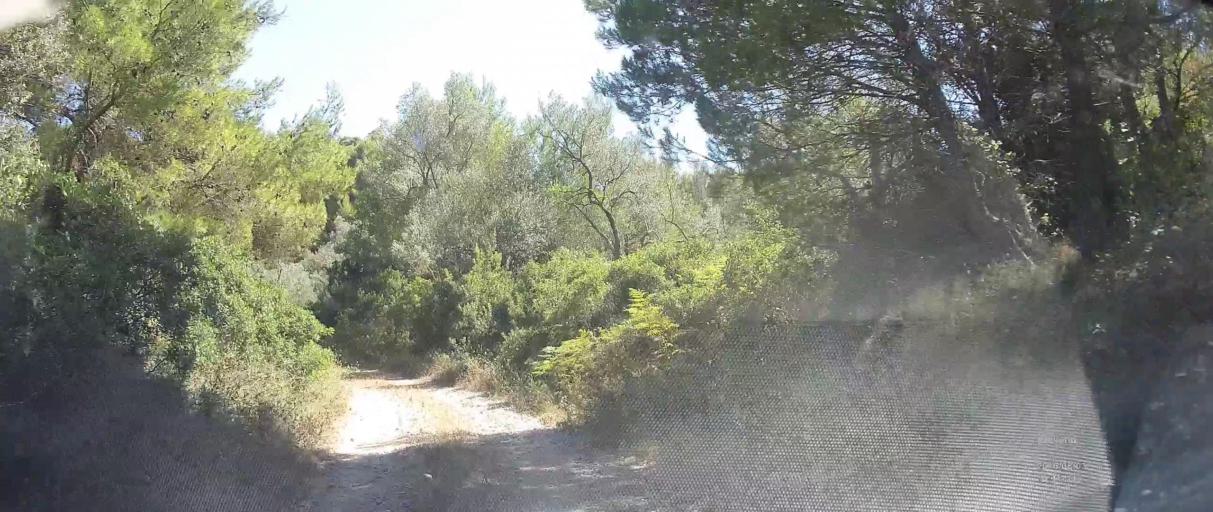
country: HR
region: Dubrovacko-Neretvanska
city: Blato
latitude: 42.7291
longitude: 17.5547
